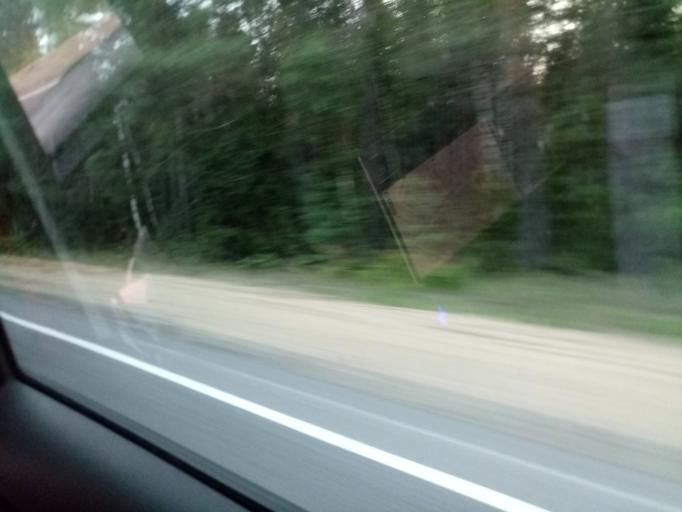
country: RU
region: Moskovskaya
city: Noginsk-9
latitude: 56.0846
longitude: 38.5773
